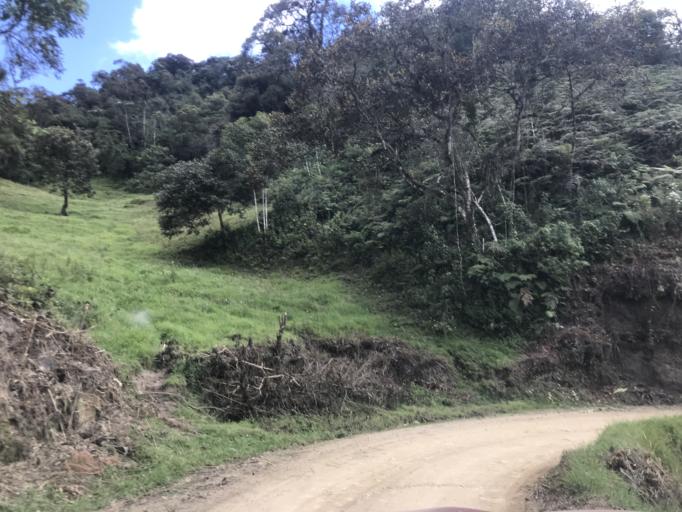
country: PE
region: Cajamarca
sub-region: Provincia de Chota
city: Querocoto
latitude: -6.3499
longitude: -79.0583
